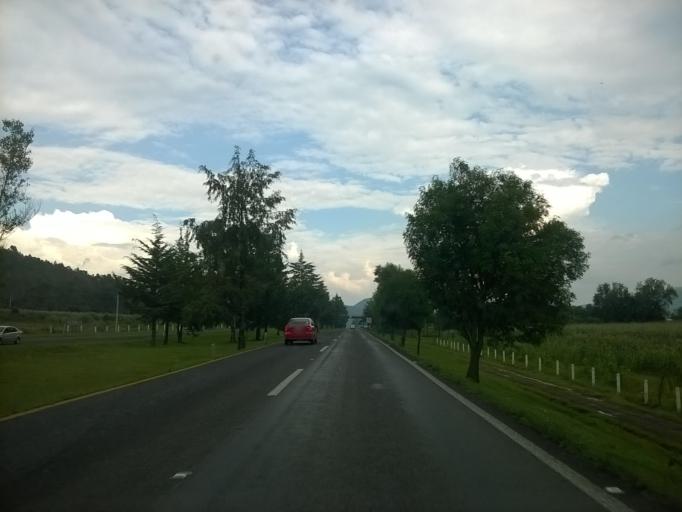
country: MX
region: Michoacan
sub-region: Huiramba
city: El Pedregal
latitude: 19.5311
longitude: -101.4861
